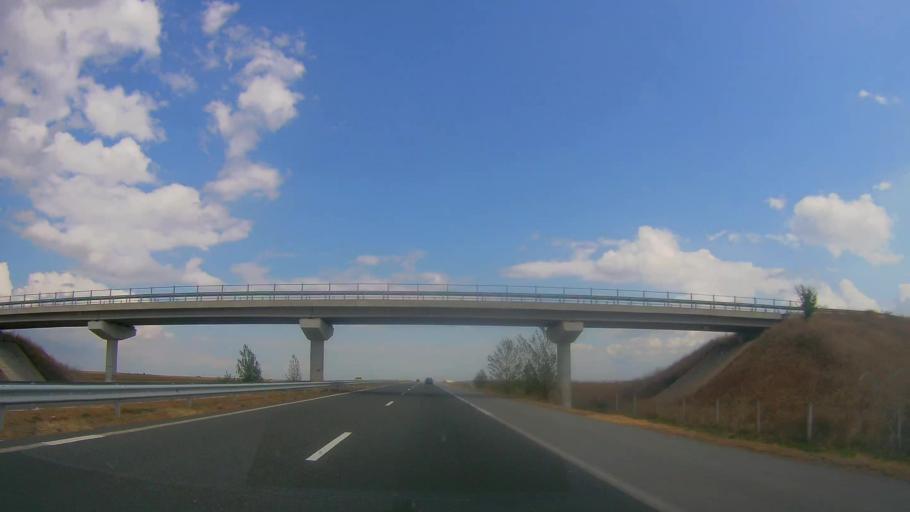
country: BG
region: Yambol
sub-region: Obshtina Yambol
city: Yambol
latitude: 42.5555
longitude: 26.5538
